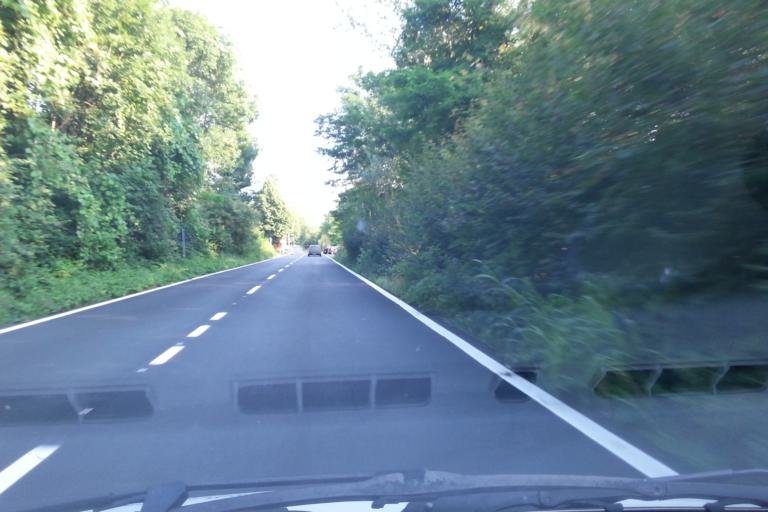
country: IT
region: Piedmont
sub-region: Provincia di Torino
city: Avigliana
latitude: 45.0560
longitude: 7.3960
